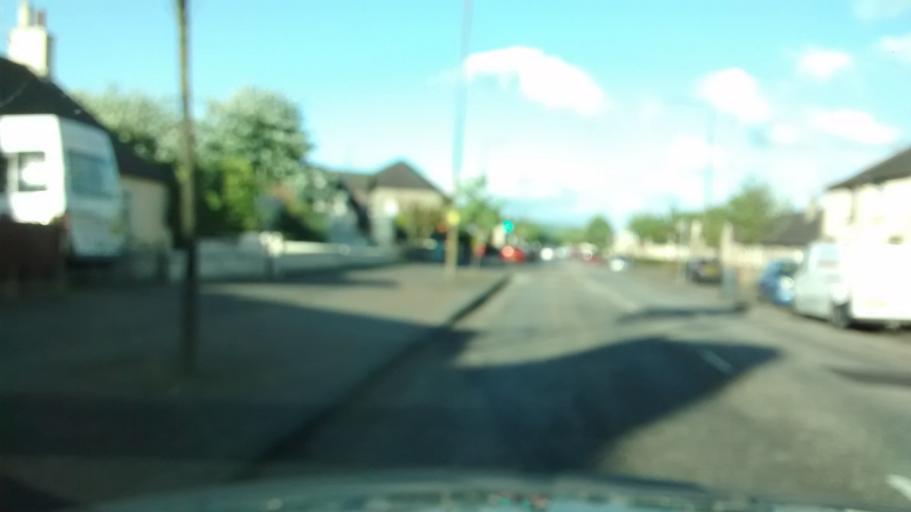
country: GB
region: Scotland
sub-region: West Lothian
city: Armadale
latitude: 55.8989
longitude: -3.6955
